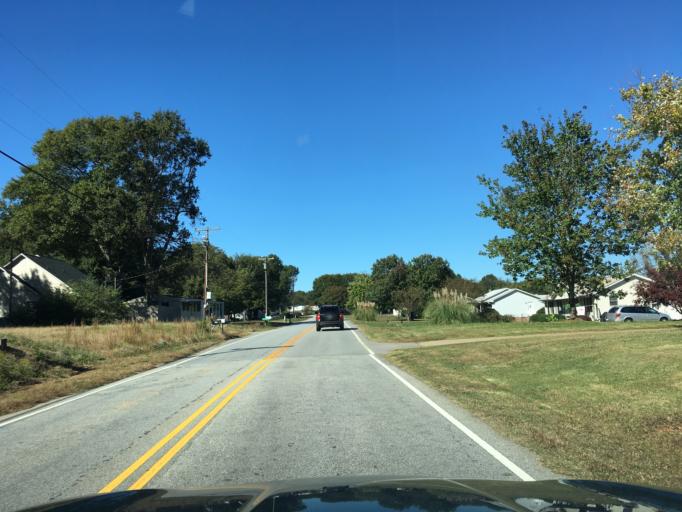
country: US
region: South Carolina
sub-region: Spartanburg County
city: Wellford
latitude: 34.8662
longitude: -82.0963
